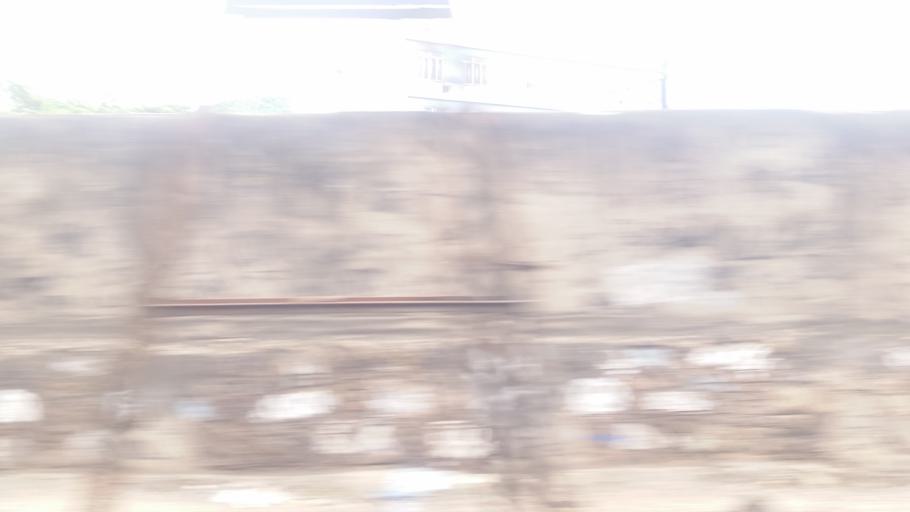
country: BR
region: Rio de Janeiro
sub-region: Sao Joao De Meriti
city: Sao Joao de Meriti
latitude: -22.8793
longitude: -43.3336
